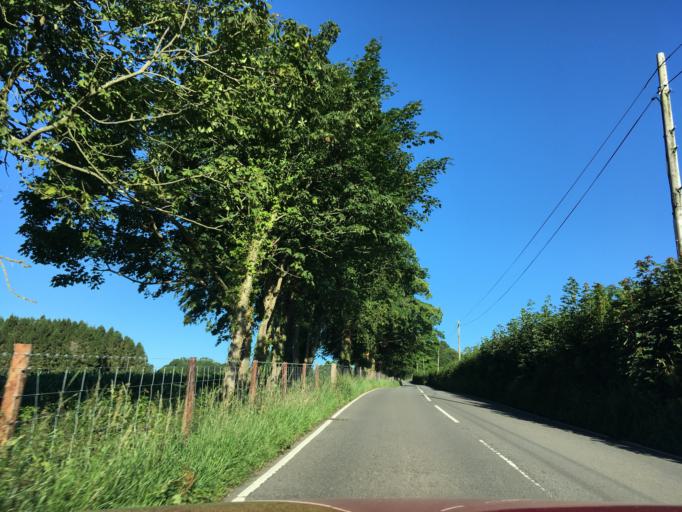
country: GB
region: Wales
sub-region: Monmouthshire
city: Chepstow
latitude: 51.6611
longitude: -2.7383
